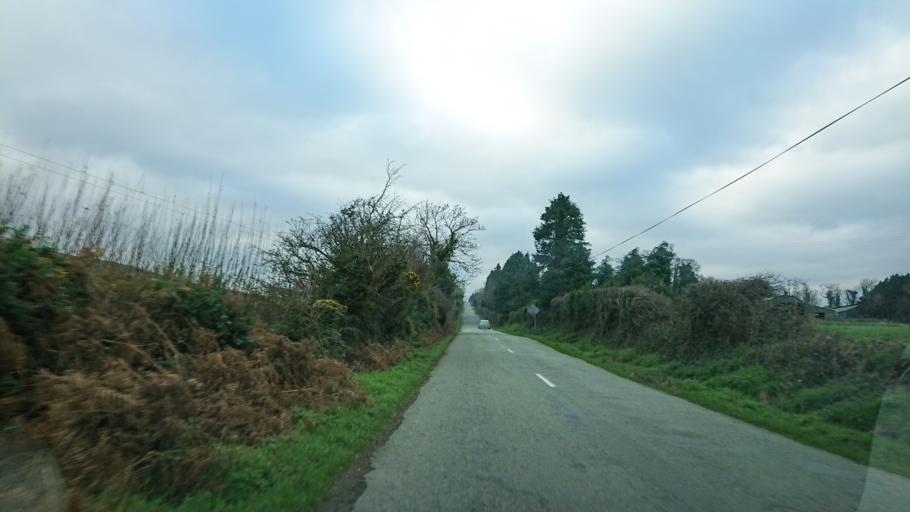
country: IE
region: Munster
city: Carrick-on-Suir
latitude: 52.3186
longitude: -7.5532
